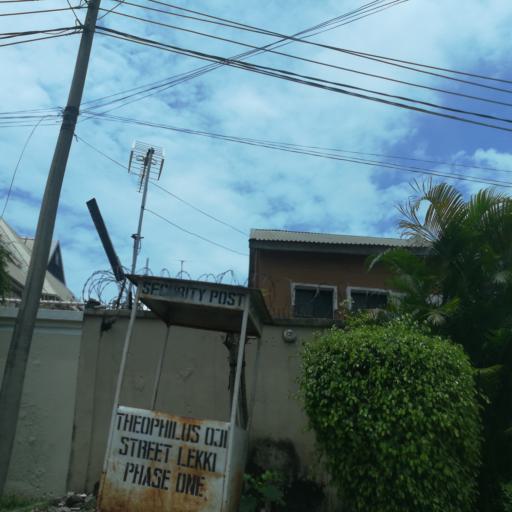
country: NG
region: Lagos
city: Ikoyi
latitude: 6.4384
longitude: 3.4650
